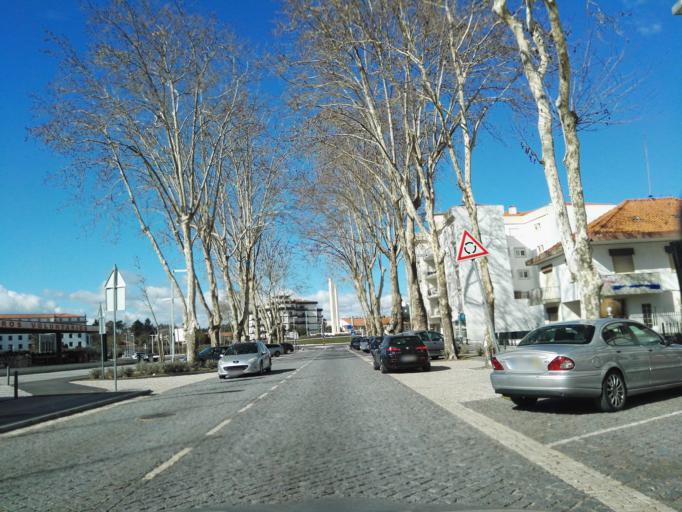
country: PT
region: Santarem
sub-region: Ourem
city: Fatima
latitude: 39.6337
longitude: -8.6820
